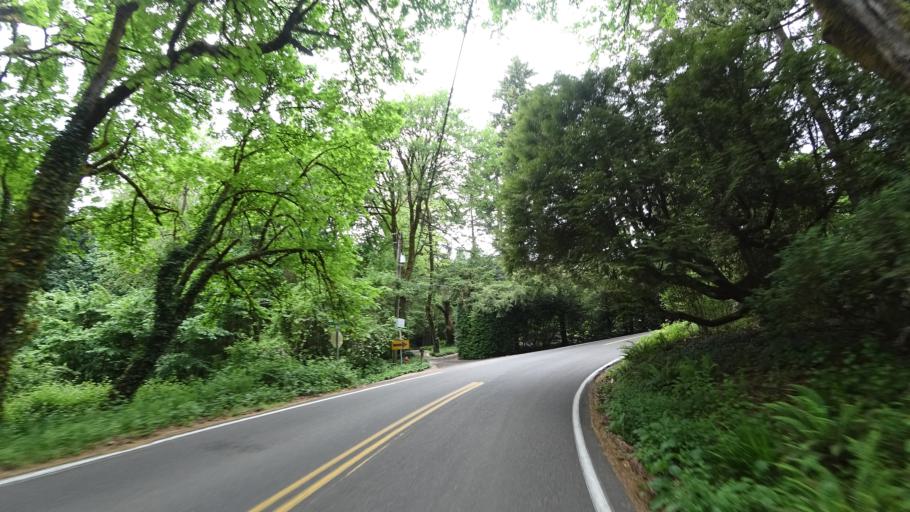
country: US
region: Oregon
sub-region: Clackamas County
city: Lake Oswego
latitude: 45.4439
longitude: -122.6640
